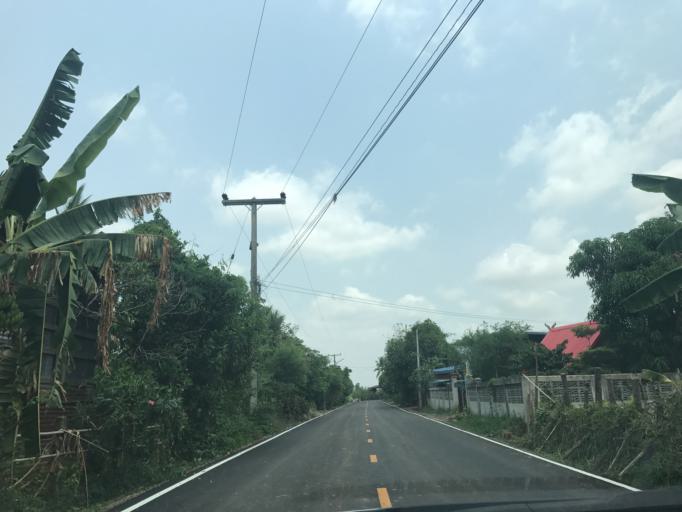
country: TH
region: Surin
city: Khwao Sinarin
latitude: 15.0404
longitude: 103.6507
